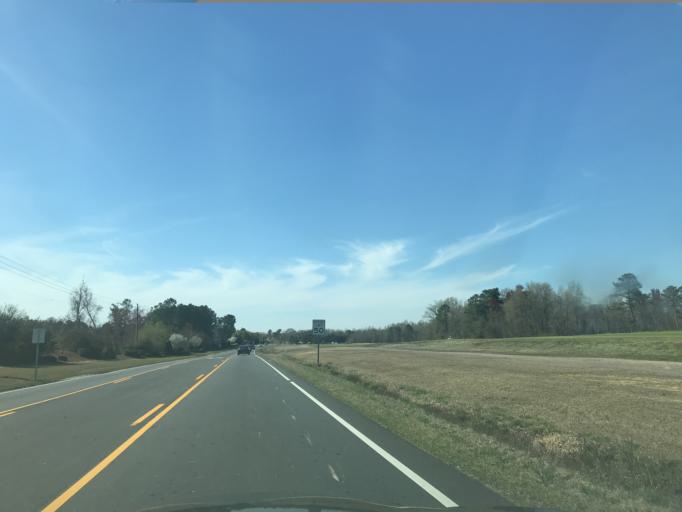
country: US
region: North Carolina
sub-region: Harnett County
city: Angier
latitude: 35.5425
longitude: -78.7502
